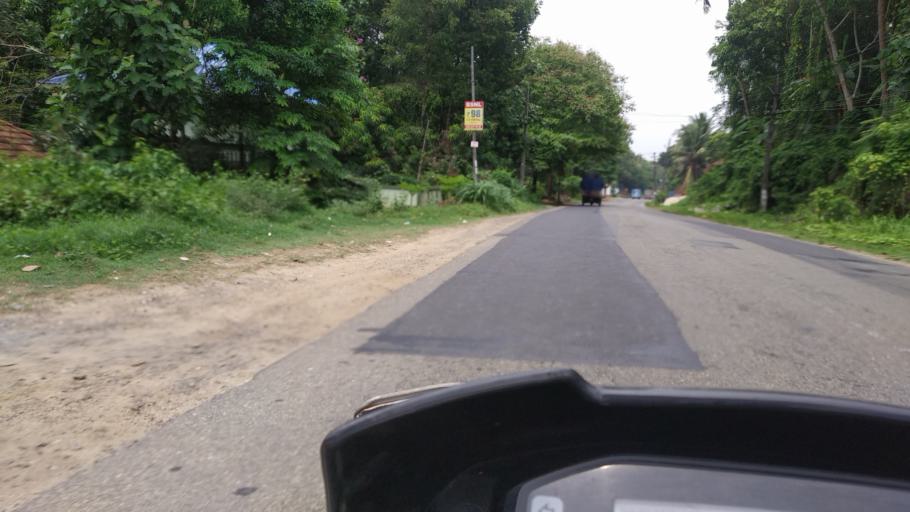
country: IN
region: Kerala
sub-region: Ernakulam
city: Perumpavur
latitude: 10.1003
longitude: 76.5443
